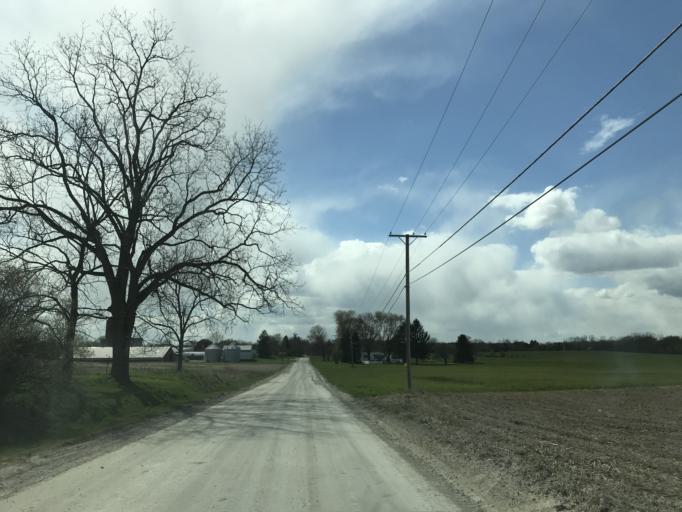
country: US
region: Michigan
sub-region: Oakland County
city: South Lyon
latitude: 42.3885
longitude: -83.6533
